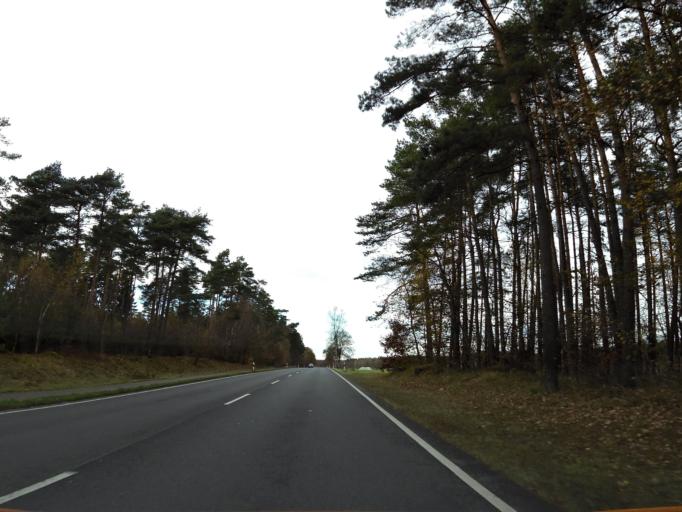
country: DE
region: Lower Saxony
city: Munster
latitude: 52.9632
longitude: 10.1136
